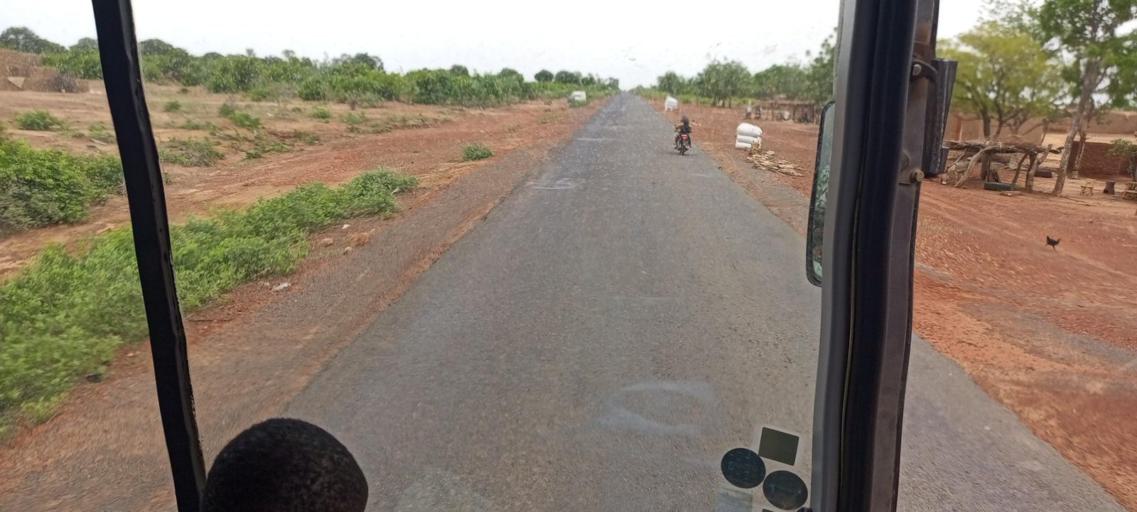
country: ML
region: Sikasso
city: Koutiala
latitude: 12.5357
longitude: -5.5709
